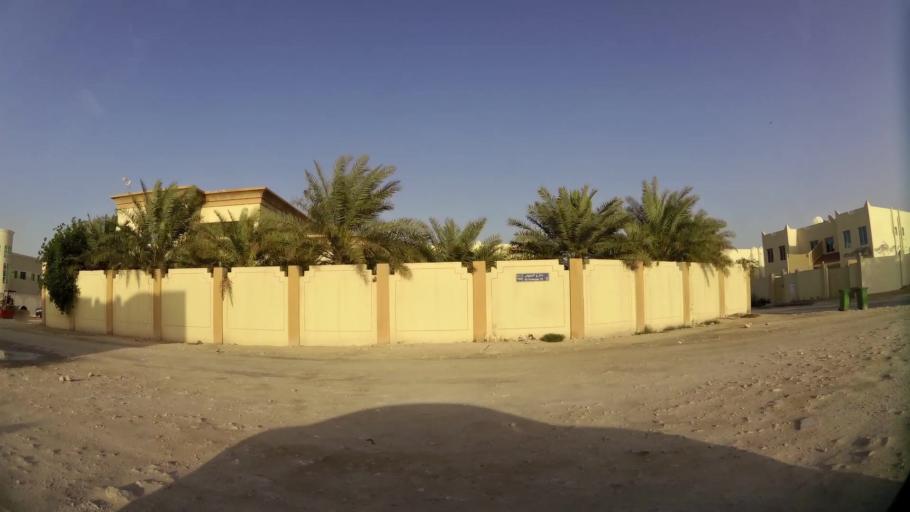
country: QA
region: Baladiyat ar Rayyan
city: Ar Rayyan
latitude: 25.3225
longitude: 51.4528
